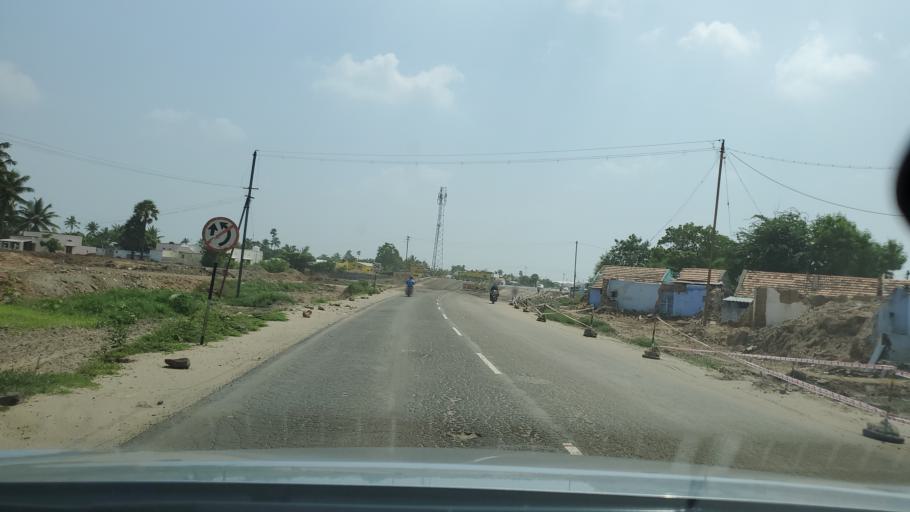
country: IN
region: Tamil Nadu
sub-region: Tiruppur
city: Dharapuram
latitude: 10.7702
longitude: 77.5120
